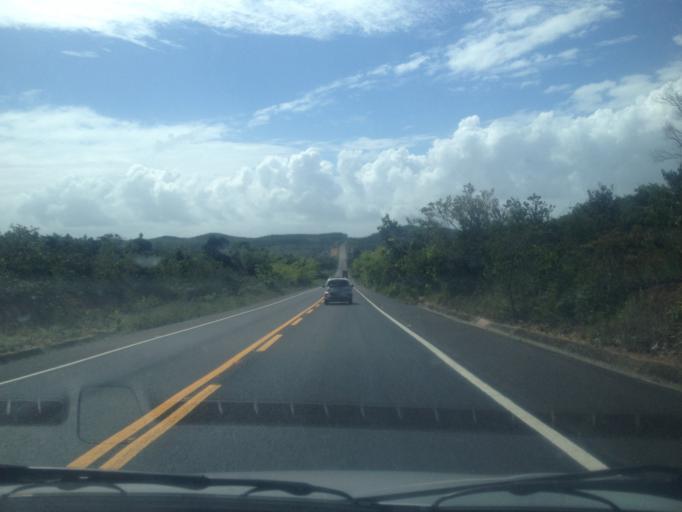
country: BR
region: Bahia
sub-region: Conde
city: Conde
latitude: -11.6822
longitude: -37.5657
